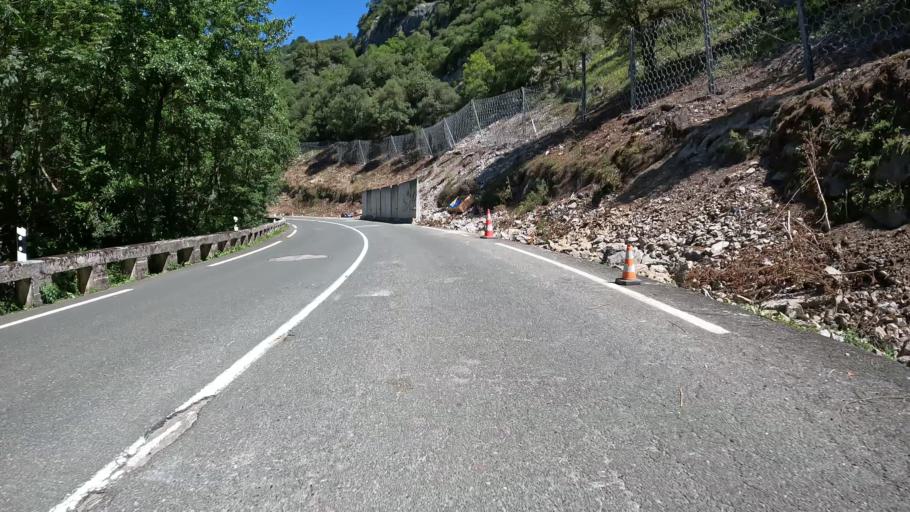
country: ES
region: Basque Country
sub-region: Provincia de Guipuzcoa
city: Oreja
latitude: 43.0784
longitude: -2.0175
